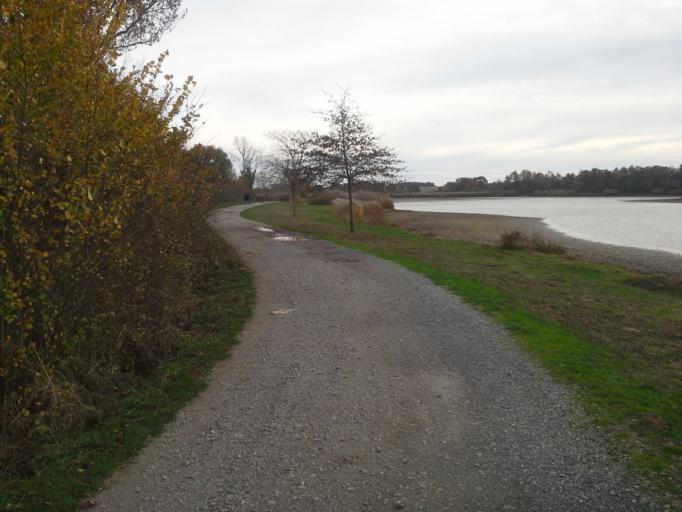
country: FR
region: Poitou-Charentes
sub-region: Departement de la Vienne
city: Pleumartin
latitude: 46.6374
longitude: 0.7637
